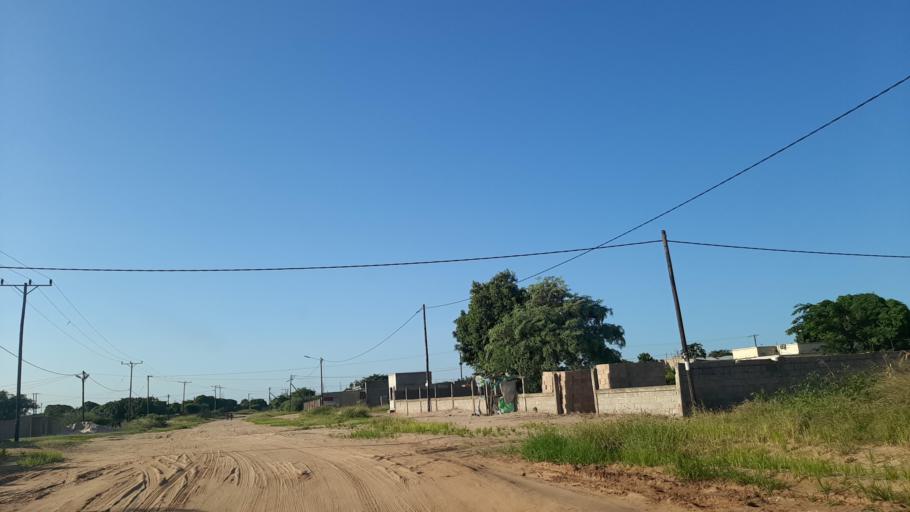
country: MZ
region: Maputo City
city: Maputo
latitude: -25.7668
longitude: 32.5477
